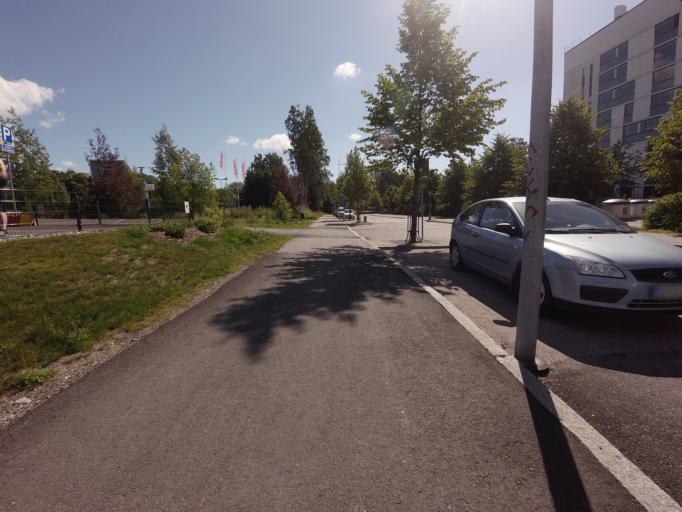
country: FI
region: Uusimaa
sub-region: Helsinki
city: Espoo
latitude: 60.1515
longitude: 24.6633
